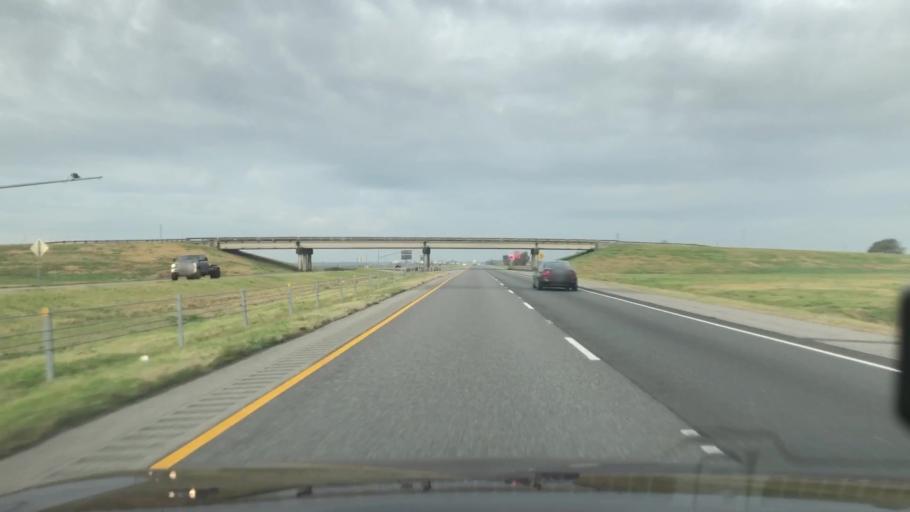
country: US
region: Mississippi
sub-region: Warren County
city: Vicksburg
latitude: 32.3254
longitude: -90.9541
